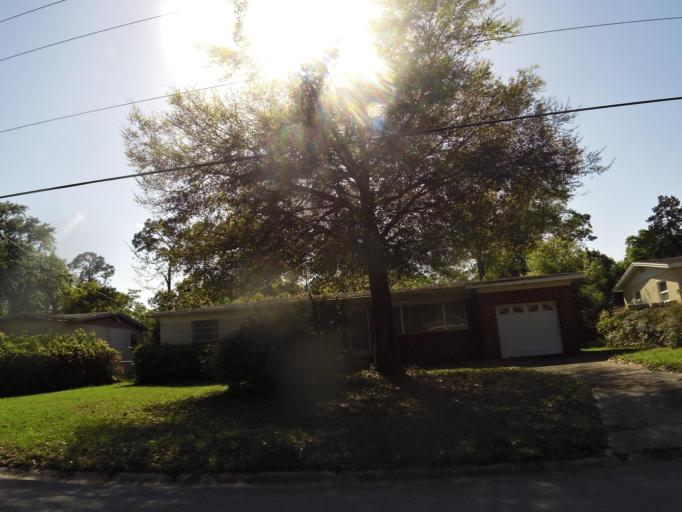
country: US
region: Florida
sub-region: Duval County
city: Jacksonville
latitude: 30.2822
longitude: -81.5956
